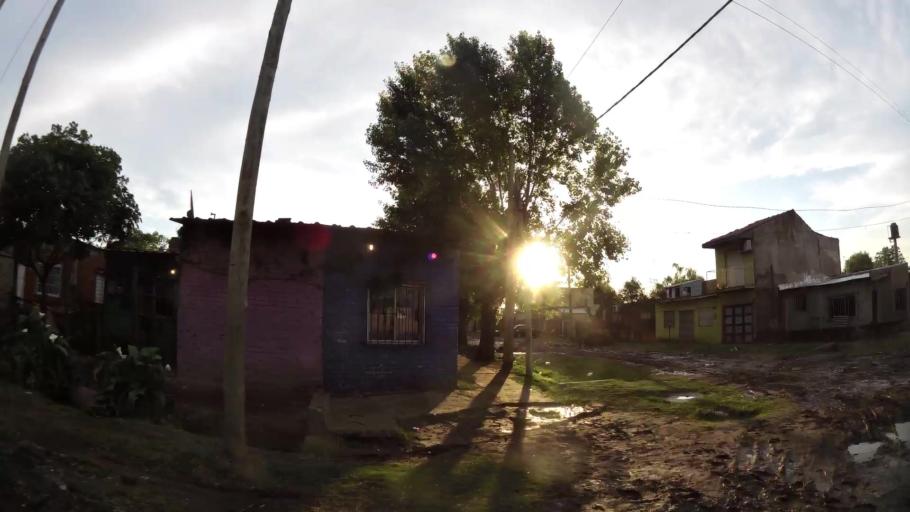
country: AR
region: Buenos Aires
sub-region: Partido de Almirante Brown
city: Adrogue
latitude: -34.7697
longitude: -58.3413
